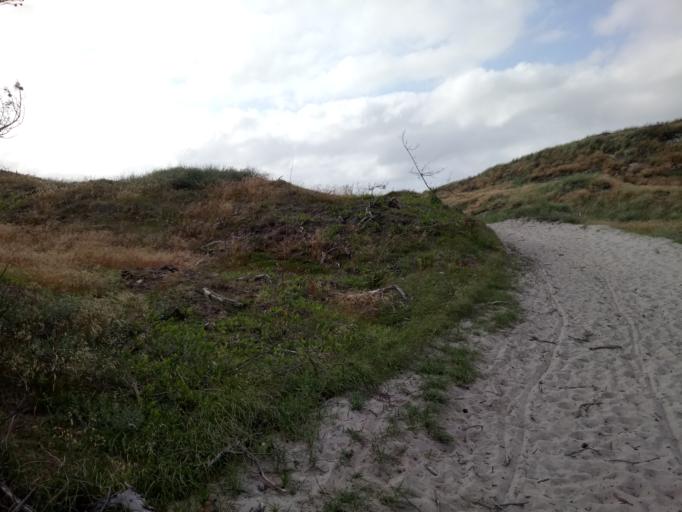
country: DK
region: Central Jutland
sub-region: Holstebro Kommune
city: Ulfborg
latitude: 56.2926
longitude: 8.1347
